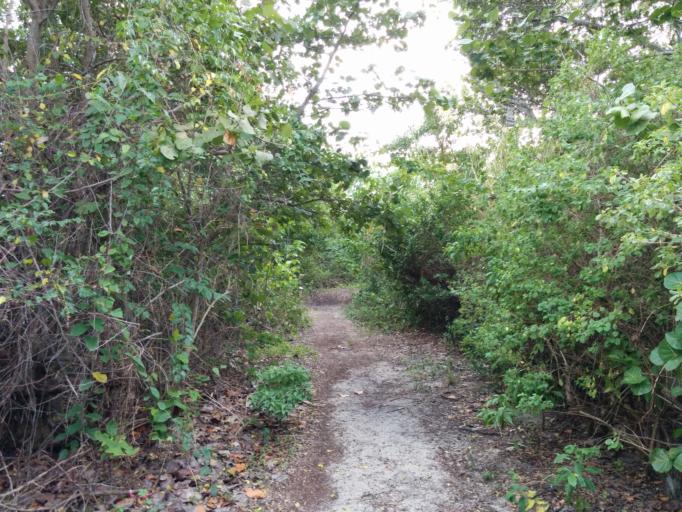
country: US
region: Florida
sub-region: Broward County
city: Dania Beach
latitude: 26.0693
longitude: -80.1123
